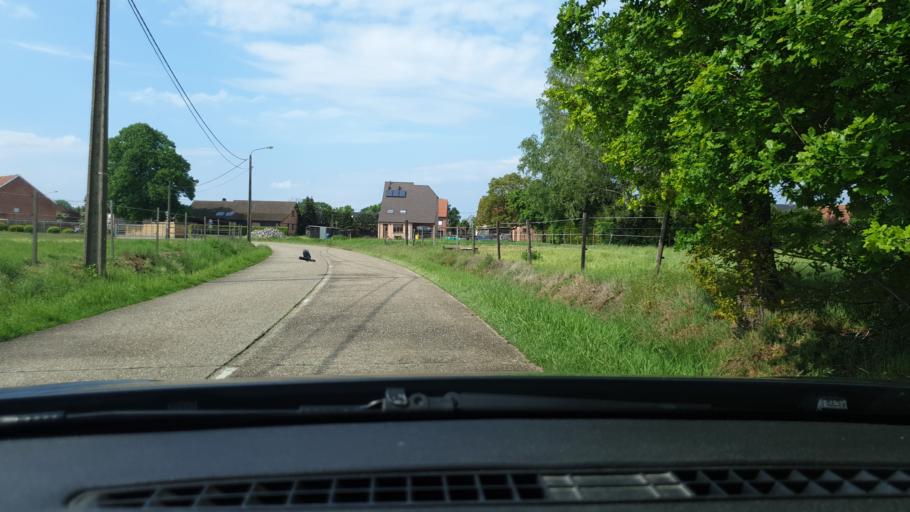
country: BE
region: Flanders
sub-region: Provincie Antwerpen
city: Meerhout
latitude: 51.1108
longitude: 5.1054
